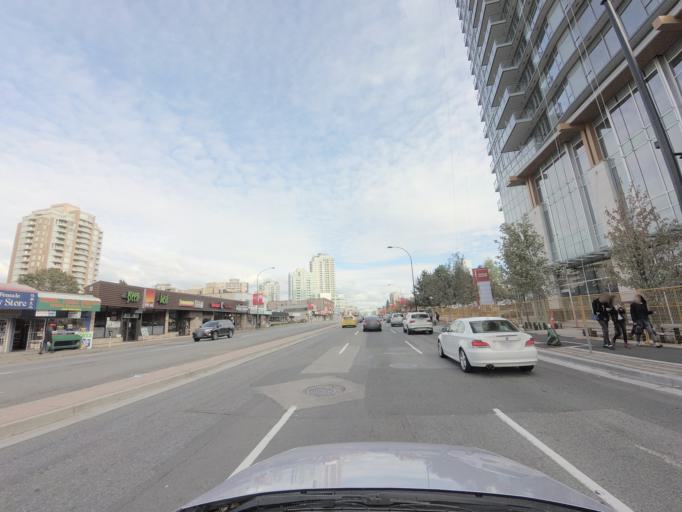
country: CA
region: British Columbia
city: Burnaby
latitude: 49.2291
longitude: -123.0015
